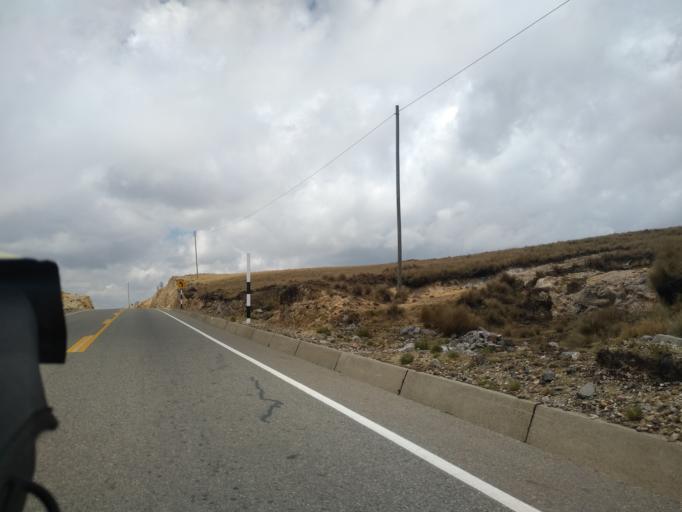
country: PE
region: La Libertad
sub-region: Provincia de Santiago de Chuco
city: Quiruvilca
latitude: -7.9556
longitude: -78.1951
